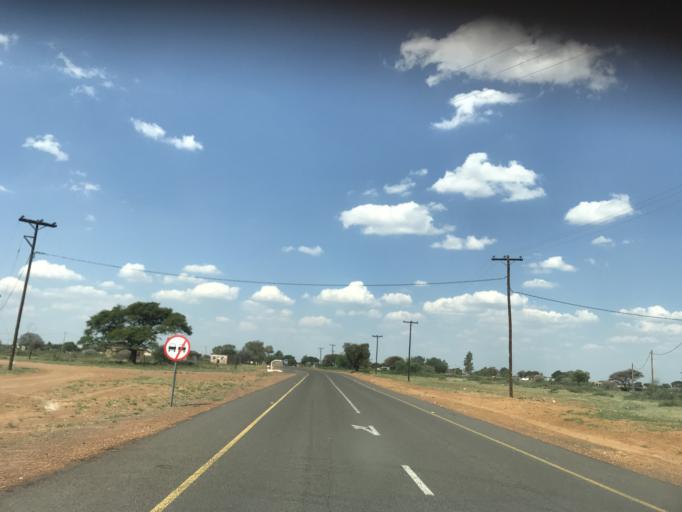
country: BW
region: South East
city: Janeng
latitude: -25.5624
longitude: 25.5909
